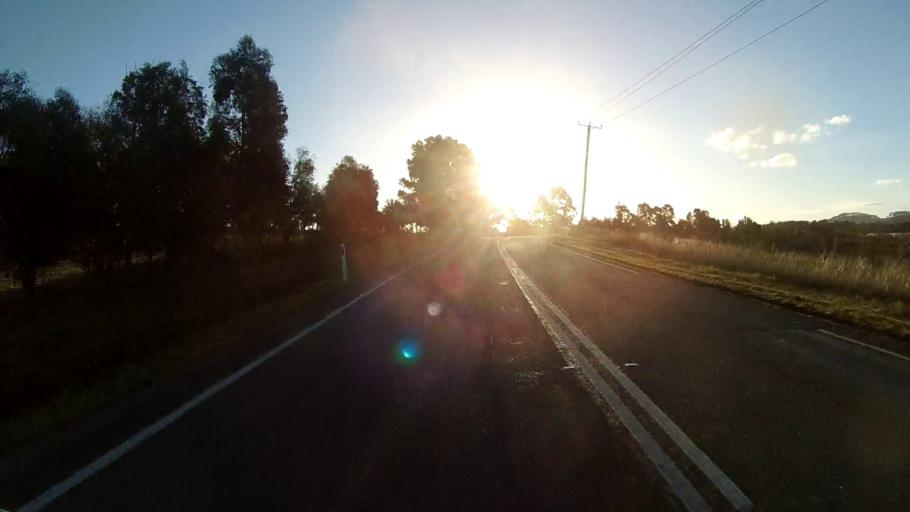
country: AU
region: Tasmania
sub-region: Sorell
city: Sorell
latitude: -42.8460
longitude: 147.8142
